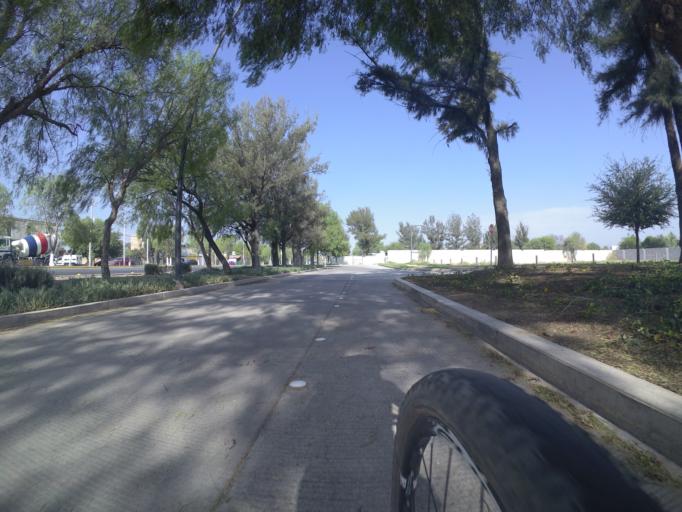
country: MX
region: Aguascalientes
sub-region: Jesus Maria
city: El Llano
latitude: 21.9497
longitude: -102.3172
